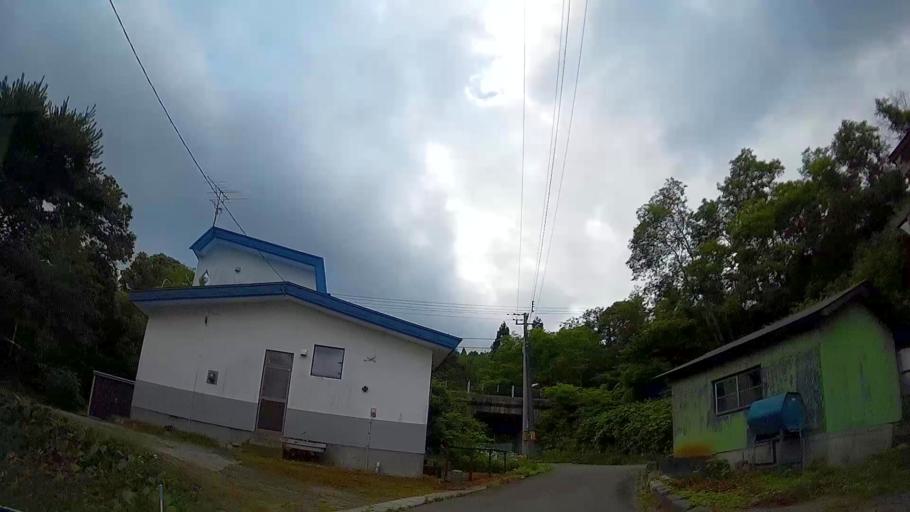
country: JP
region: Hokkaido
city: Nanae
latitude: 42.1183
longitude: 140.5373
